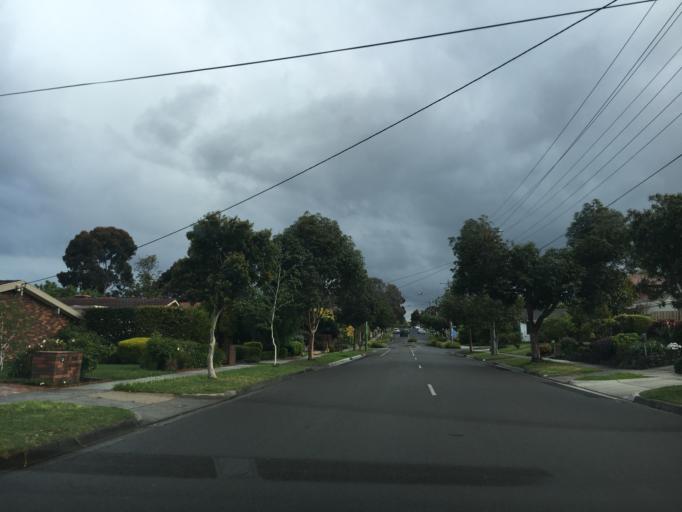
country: AU
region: Victoria
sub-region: Whitehorse
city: Vermont South
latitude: -37.8773
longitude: 145.1851
